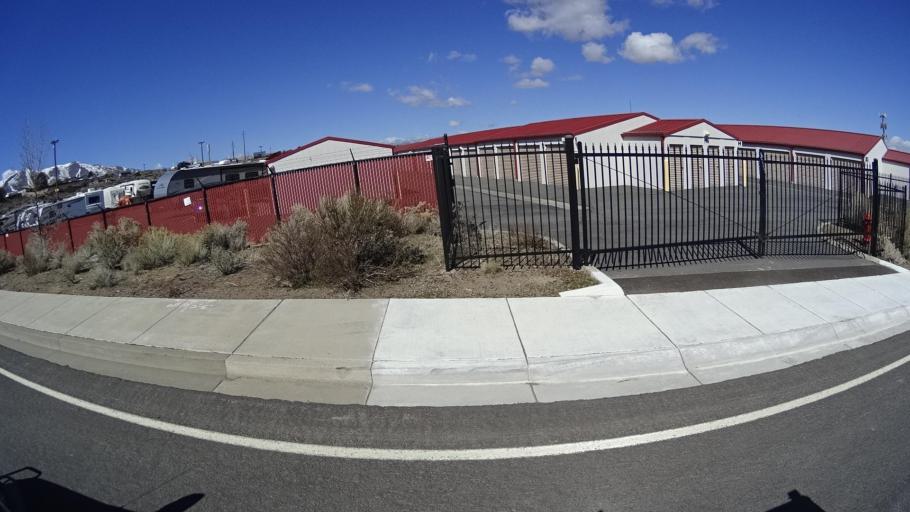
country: US
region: Nevada
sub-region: Washoe County
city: Golden Valley
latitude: 39.5954
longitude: -119.8401
